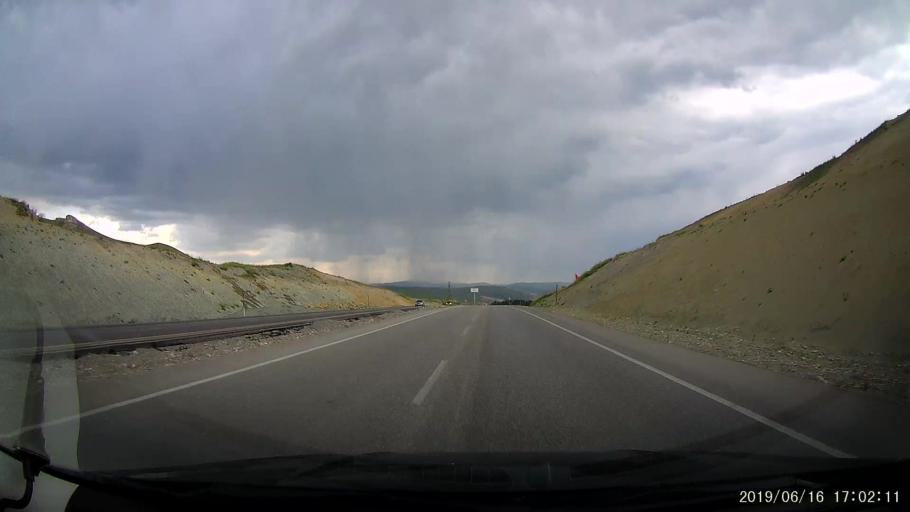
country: TR
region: Erzurum
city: Askale
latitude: 39.9421
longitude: 40.7598
